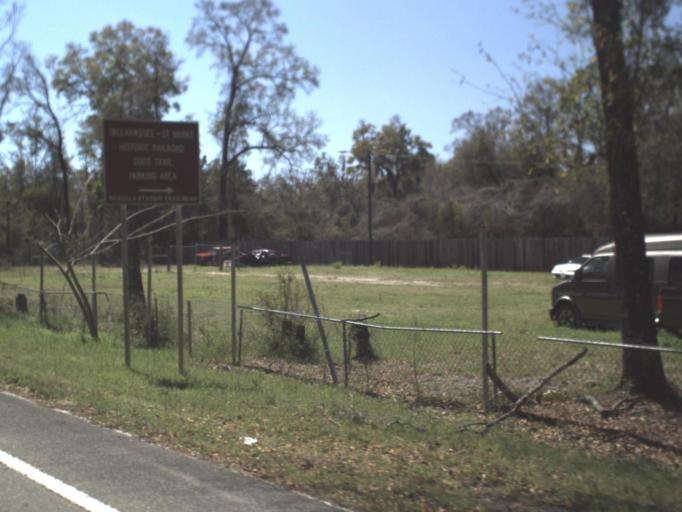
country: US
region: Florida
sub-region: Leon County
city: Woodville
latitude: 30.2496
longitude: -84.2337
